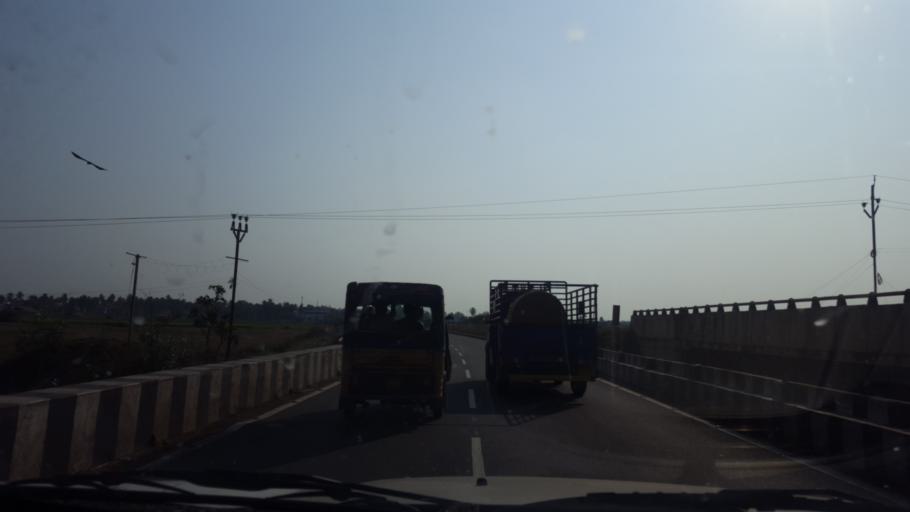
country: IN
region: Andhra Pradesh
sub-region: Vishakhapatnam
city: Etikoppaka
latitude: 17.4402
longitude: 82.7518
